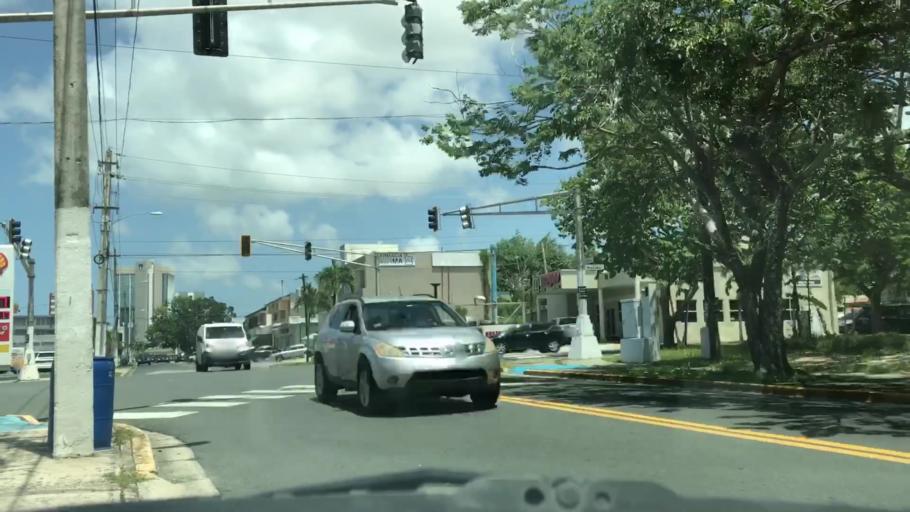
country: PR
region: Catano
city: Catano
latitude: 18.4146
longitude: -66.0621
